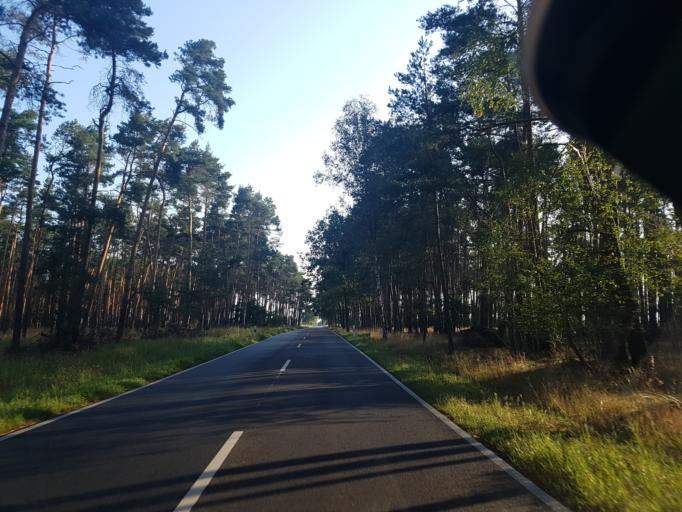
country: DE
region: Saxony-Anhalt
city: Holzdorf
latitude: 51.8050
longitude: 13.1382
